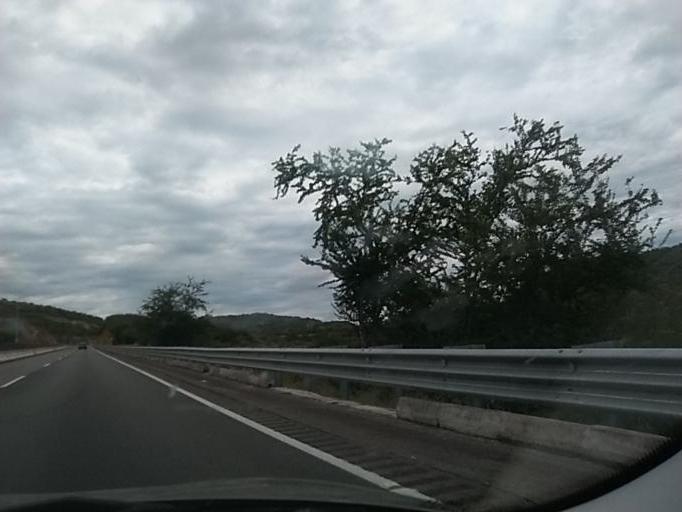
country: MX
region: Guerrero
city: Copalillo
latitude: 18.1026
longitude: -99.2087
